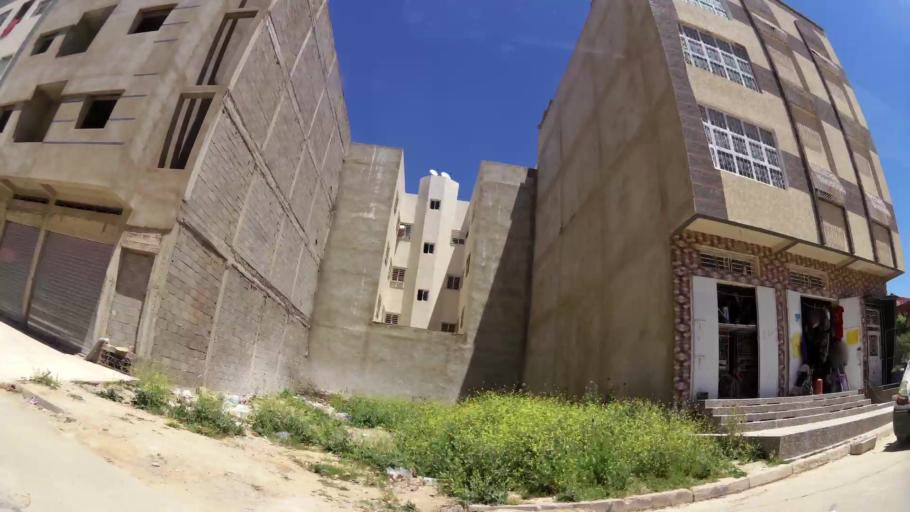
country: MA
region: Meknes-Tafilalet
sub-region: Meknes
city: Meknes
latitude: 33.8544
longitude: -5.5634
